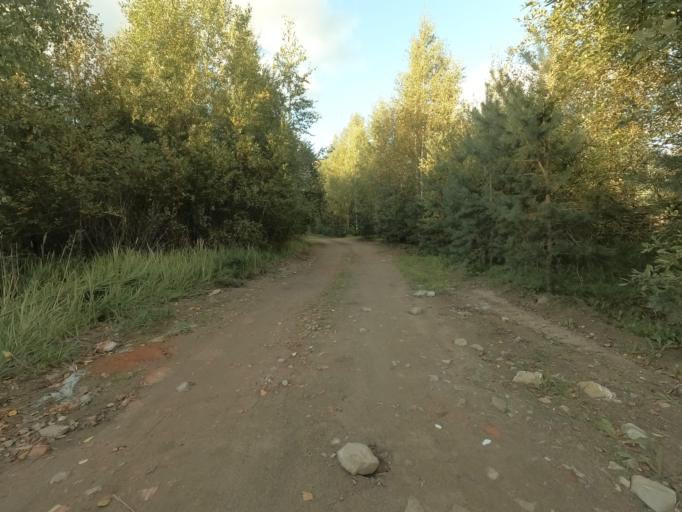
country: RU
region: Leningrad
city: Imeni Sverdlova
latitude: 59.8557
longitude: 30.7318
